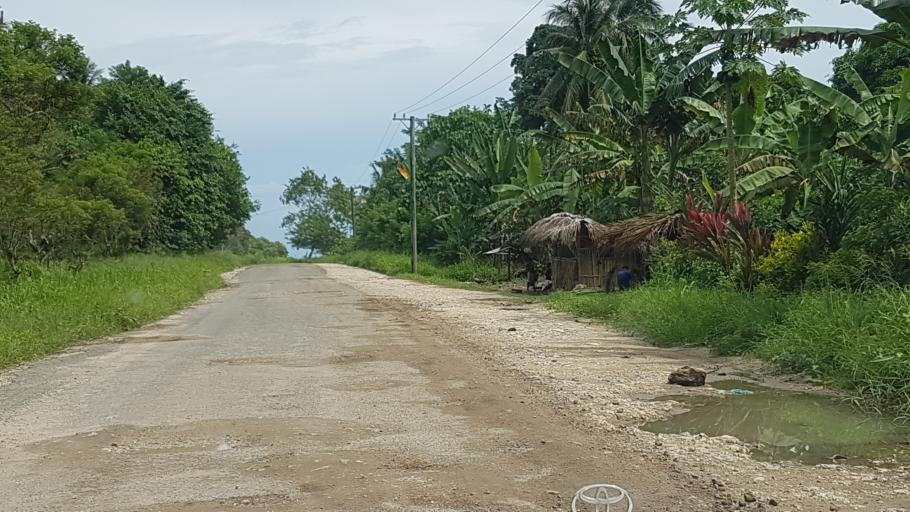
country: PG
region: Madang
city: Madang
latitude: -4.7886
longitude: 145.7156
